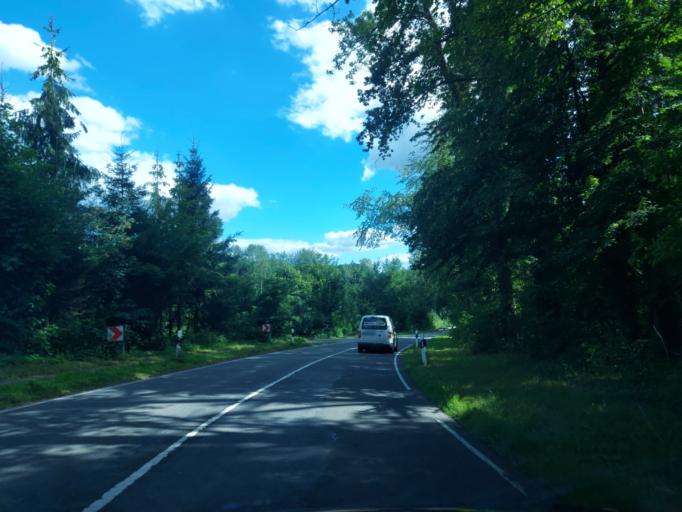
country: DE
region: Lower Saxony
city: Bad Iburg
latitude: 52.1696
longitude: 8.0422
